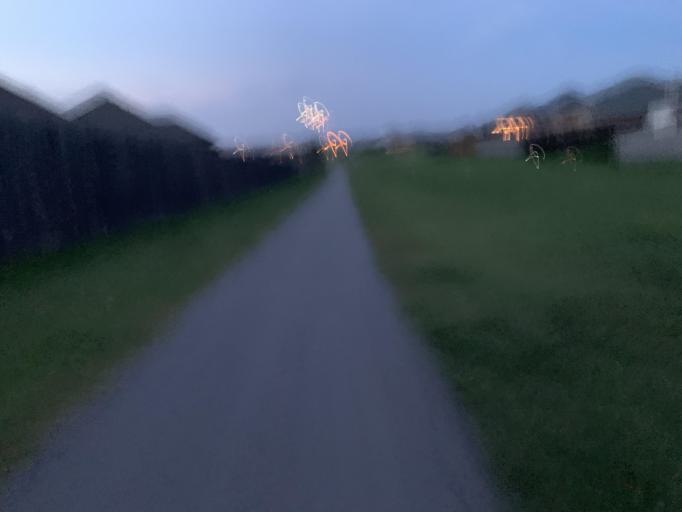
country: US
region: Oklahoma
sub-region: Oklahoma County
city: Edmond
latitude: 35.6615
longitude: -97.5738
